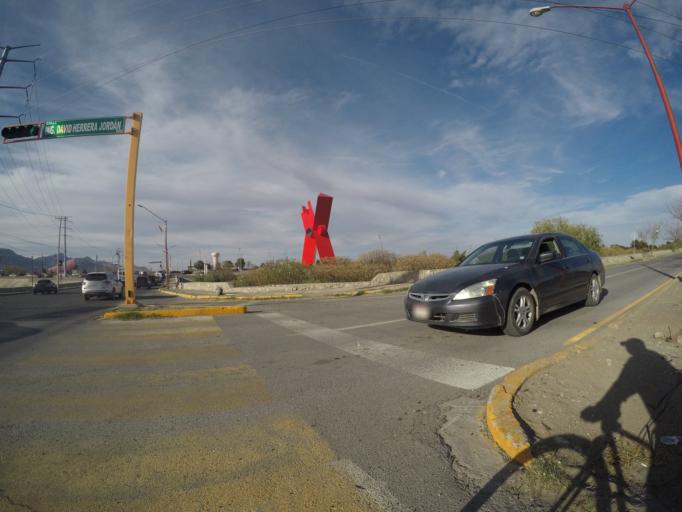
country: US
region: Texas
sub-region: El Paso County
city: El Paso
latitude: 31.7542
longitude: -106.4413
